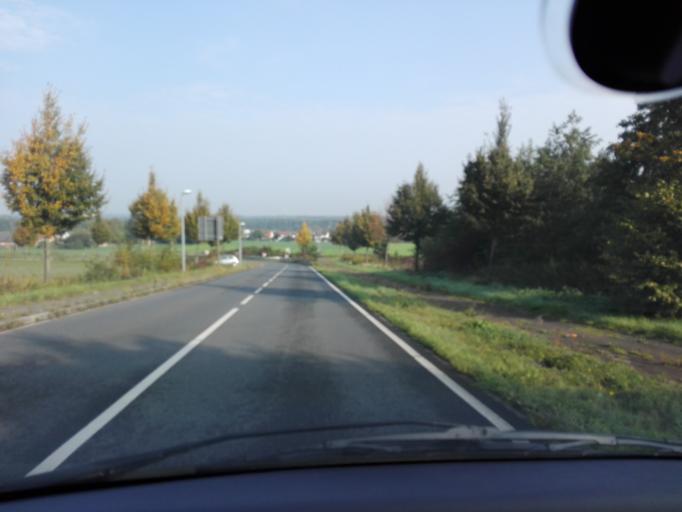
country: DE
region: North Rhine-Westphalia
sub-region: Regierungsbezirk Arnsberg
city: Unna
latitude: 51.5370
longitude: 7.7271
